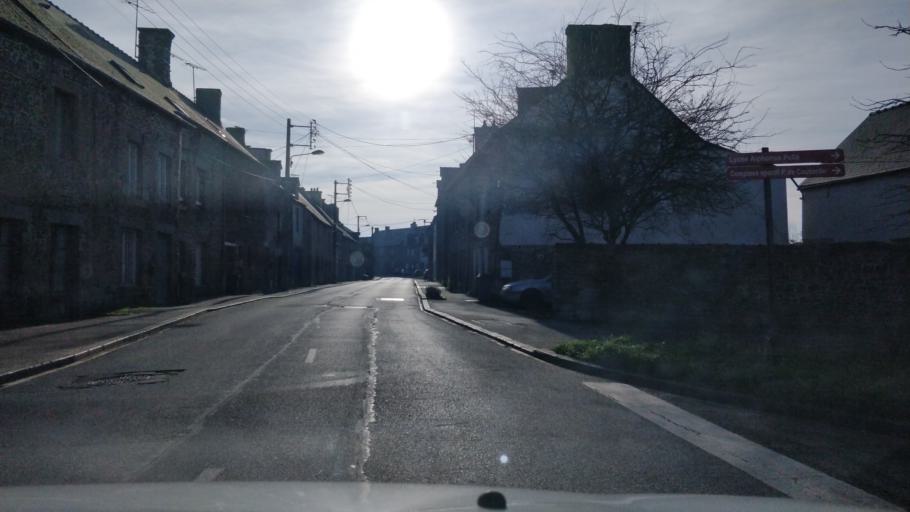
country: FR
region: Brittany
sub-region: Departement d'Ille-et-Vilaine
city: Dol-de-Bretagne
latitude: 48.5449
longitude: -1.7599
